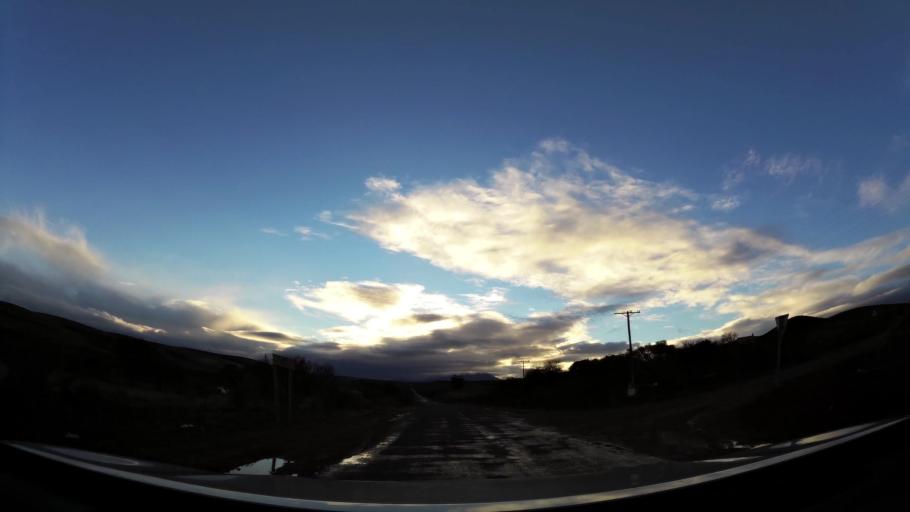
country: ZA
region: Western Cape
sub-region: Eden District Municipality
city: Riversdale
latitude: -34.0632
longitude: 20.8859
